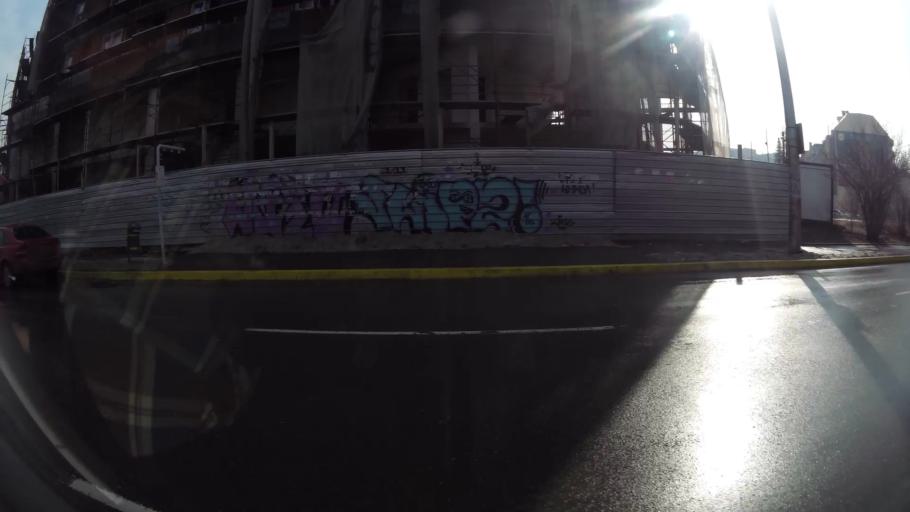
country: BG
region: Sofiya
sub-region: Obshtina Bozhurishte
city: Bozhurishte
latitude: 42.7239
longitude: 23.2591
